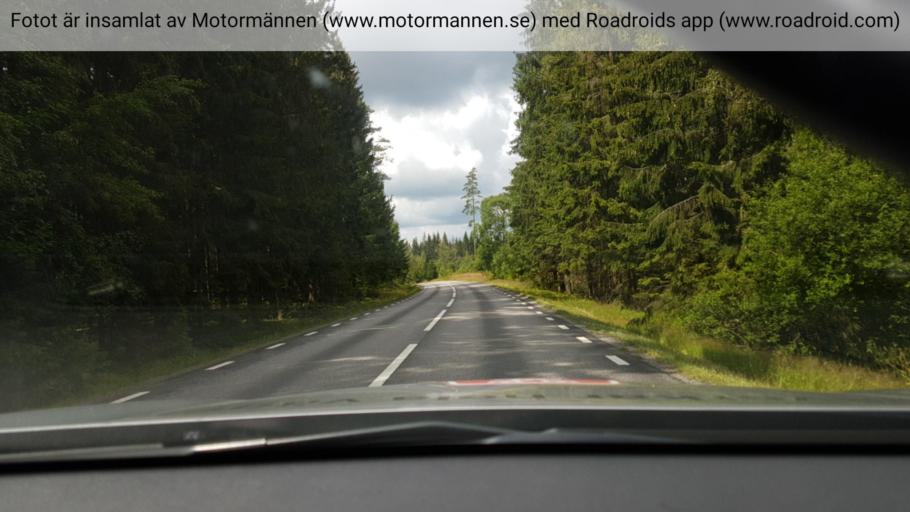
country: SE
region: Vaestra Goetaland
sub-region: Svenljunga Kommun
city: Svenljunga
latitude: 57.4790
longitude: 13.1583
